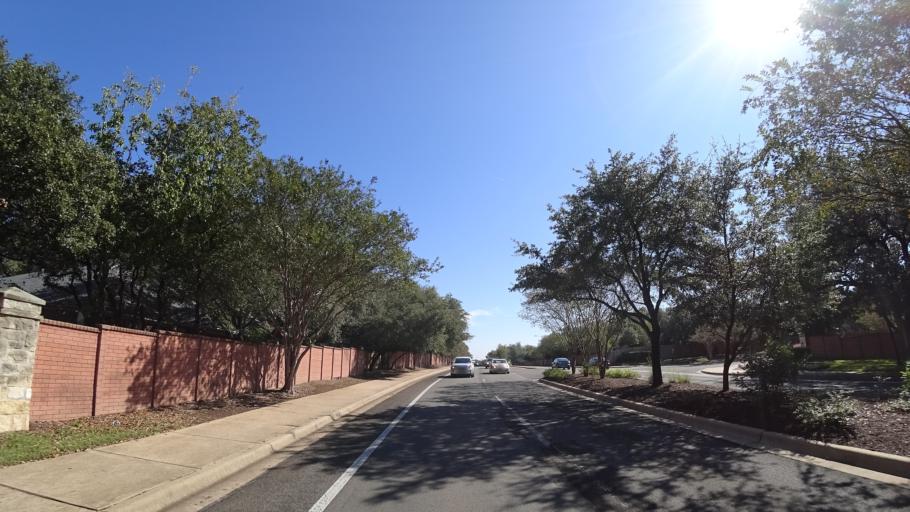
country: US
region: Texas
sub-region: Travis County
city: Shady Hollow
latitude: 30.2103
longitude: -97.8724
